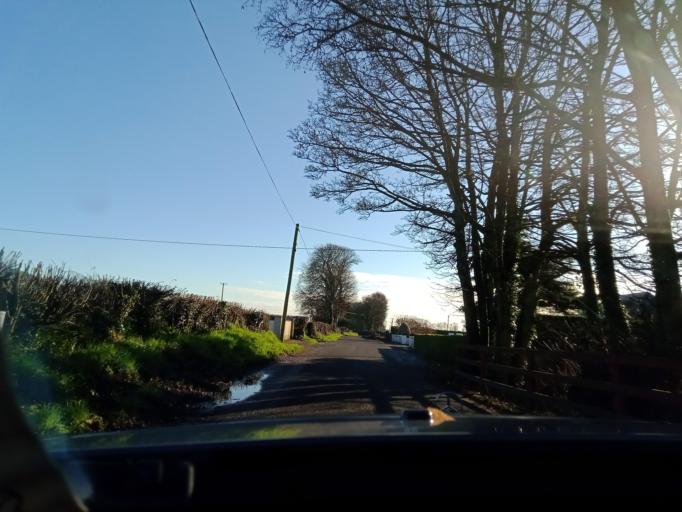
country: IE
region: Leinster
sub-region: Kilkenny
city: Piltown
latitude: 52.3644
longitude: -7.3191
